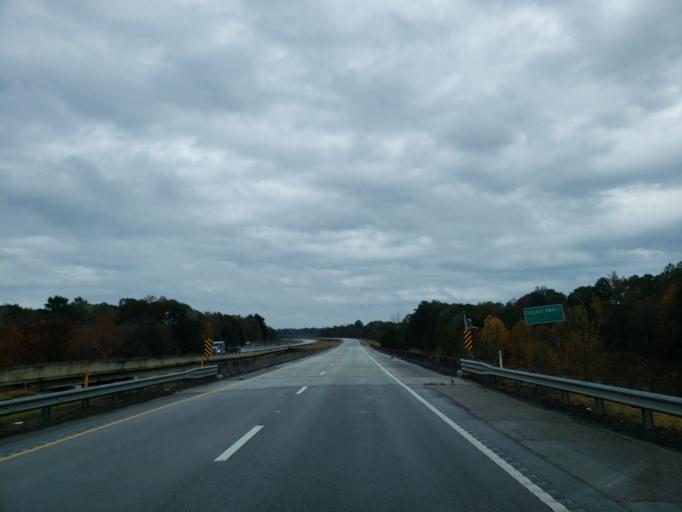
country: US
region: Mississippi
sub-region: Wayne County
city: Waynesboro
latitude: 31.6824
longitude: -88.6845
